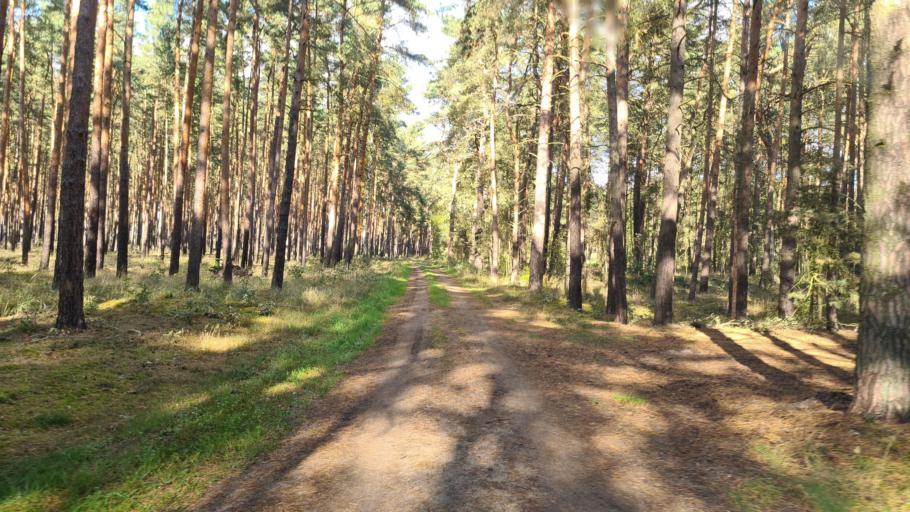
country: DE
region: Brandenburg
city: Vetschau
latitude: 51.7207
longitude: 14.0879
